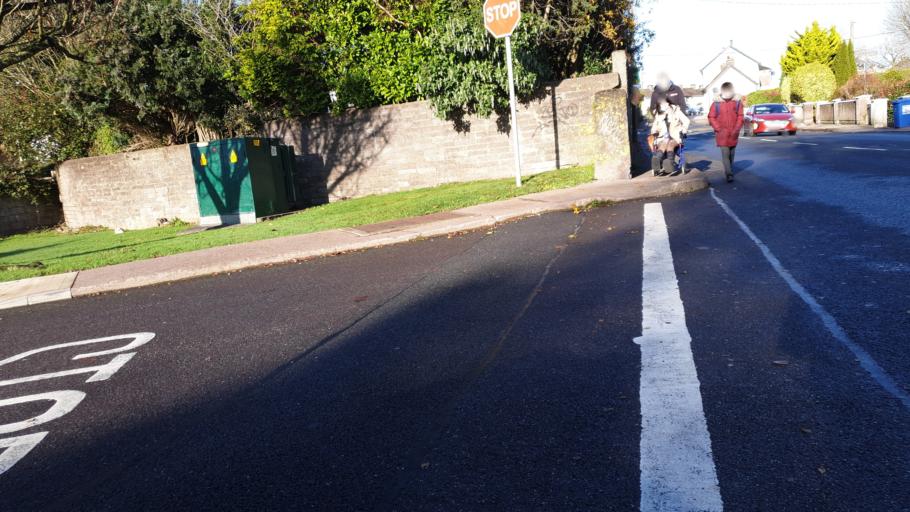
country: IE
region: Munster
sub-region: County Cork
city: Cork
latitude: 51.8894
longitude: -8.4190
